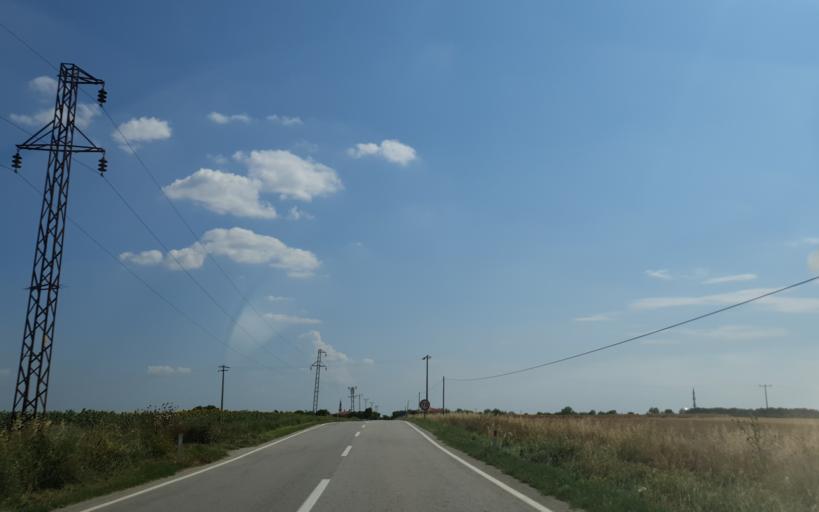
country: TR
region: Kirklareli
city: Buyukkaristiran
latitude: 41.3401
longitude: 27.5454
